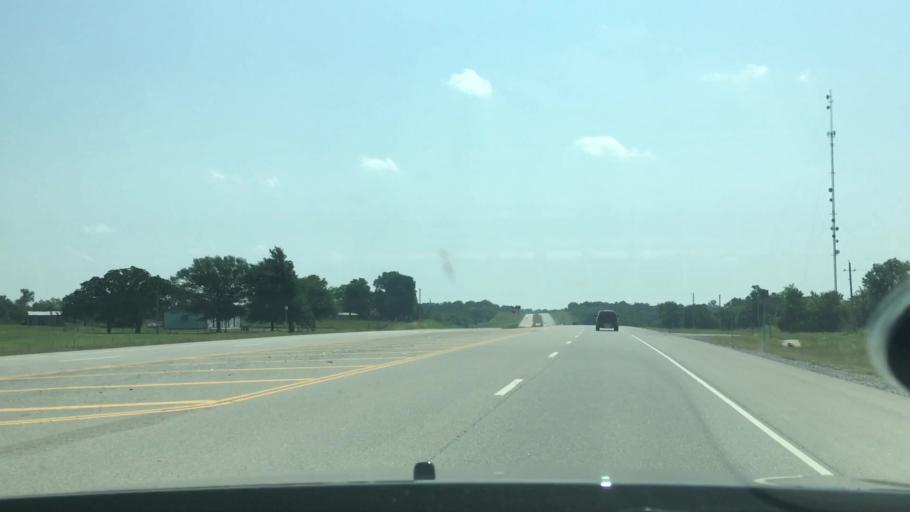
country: US
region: Oklahoma
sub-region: Atoka County
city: Atoka
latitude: 34.3585
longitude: -96.0931
